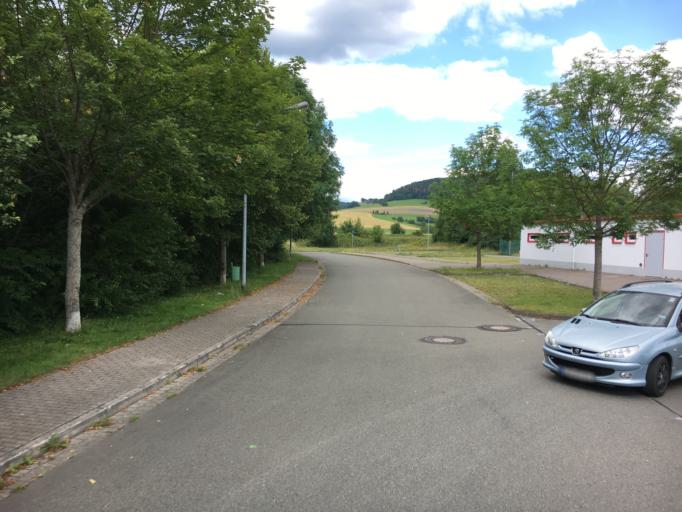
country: DE
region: Thuringia
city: Schmalkalden
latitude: 50.7260
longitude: 10.4746
